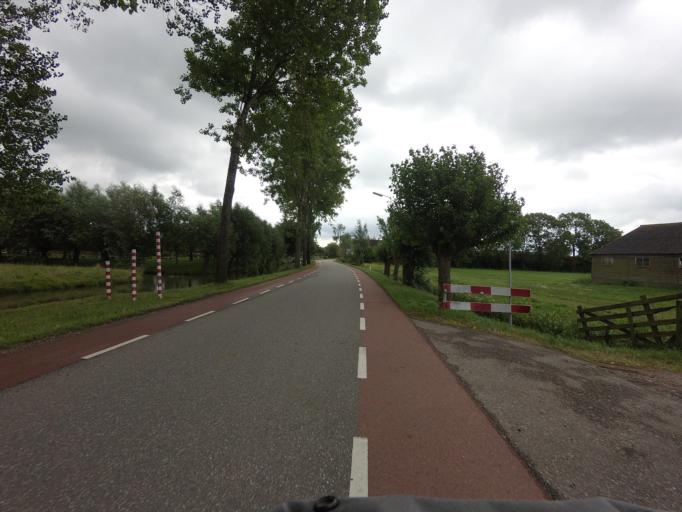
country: NL
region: Utrecht
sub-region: Gemeente IJsselstein
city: IJsselstein
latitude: 52.0490
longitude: 5.0370
